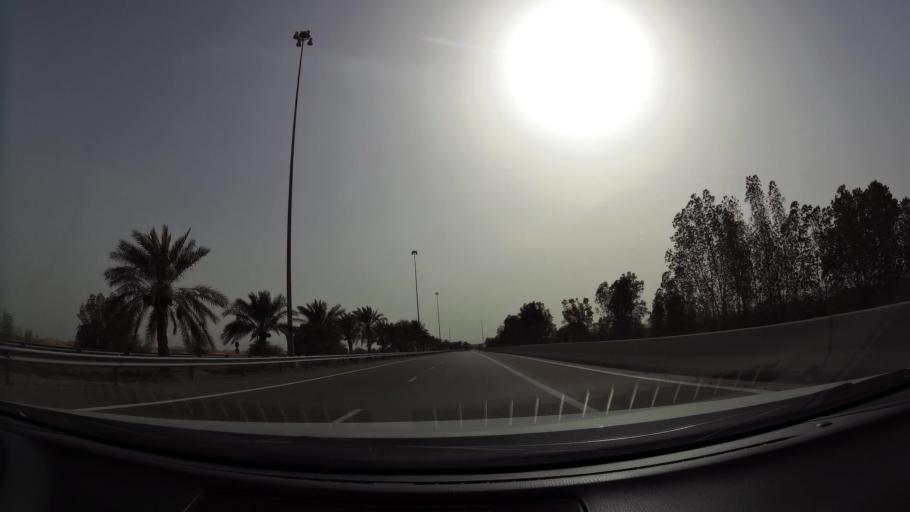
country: AE
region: Abu Dhabi
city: Al Ain
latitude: 24.1997
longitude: 55.5834
